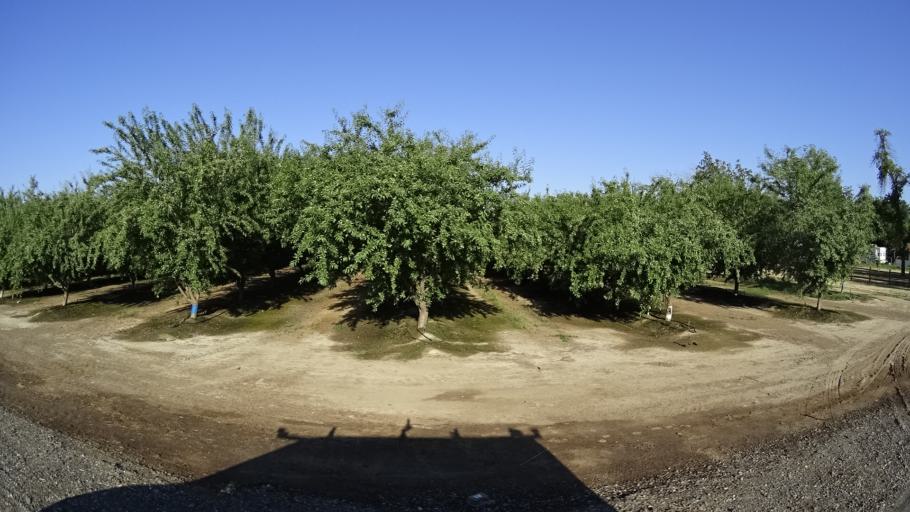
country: US
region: California
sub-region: Kings County
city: Lemoore
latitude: 36.2861
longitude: -119.7447
